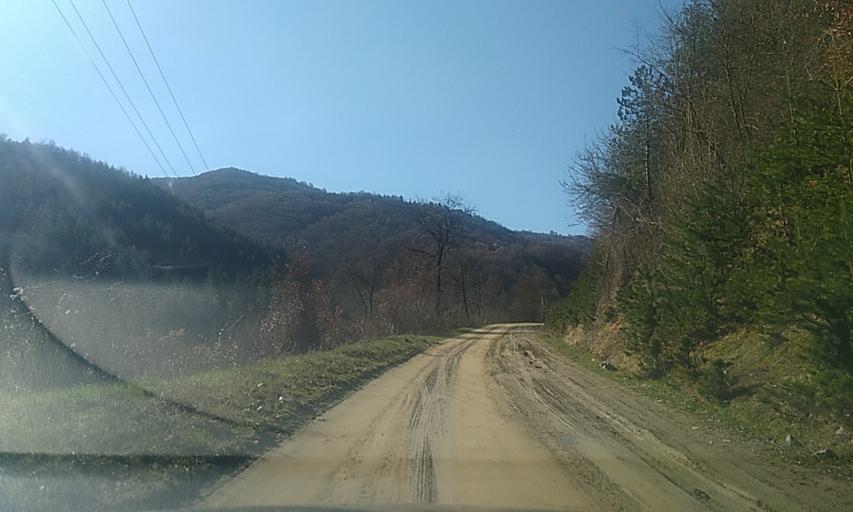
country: RS
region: Central Serbia
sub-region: Pcinjski Okrug
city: Bosilegrad
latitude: 42.3729
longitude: 22.4378
